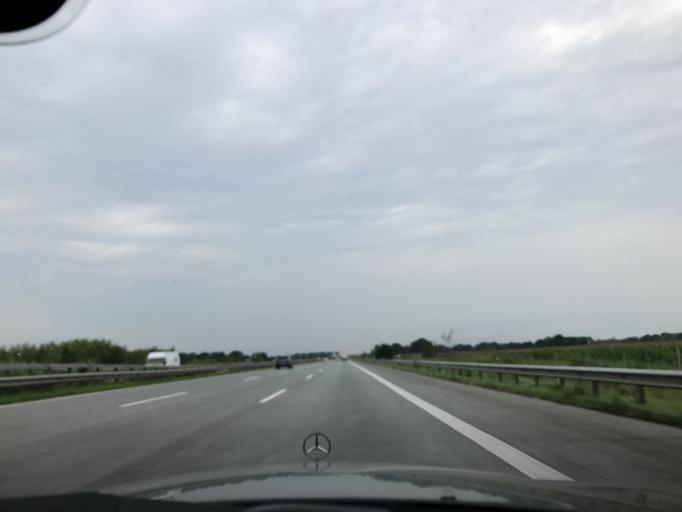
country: DE
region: Lower Saxony
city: Elsdorf
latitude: 53.2390
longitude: 9.3824
